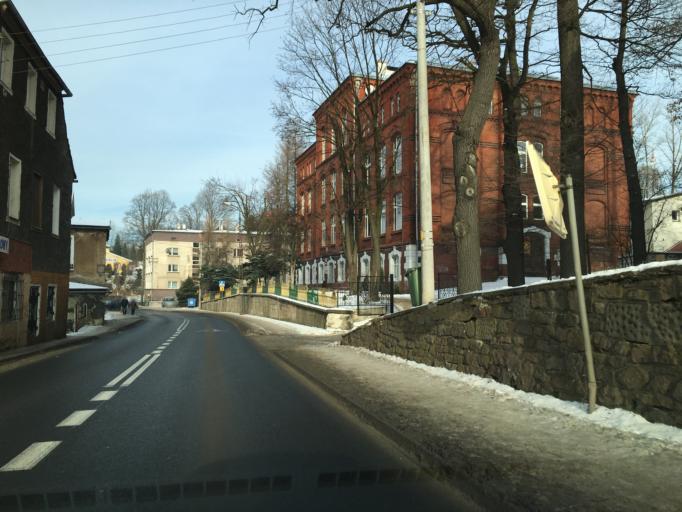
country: PL
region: Lower Silesian Voivodeship
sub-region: Powiat walbrzyski
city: Gluszyca
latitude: 50.6811
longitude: 16.3787
